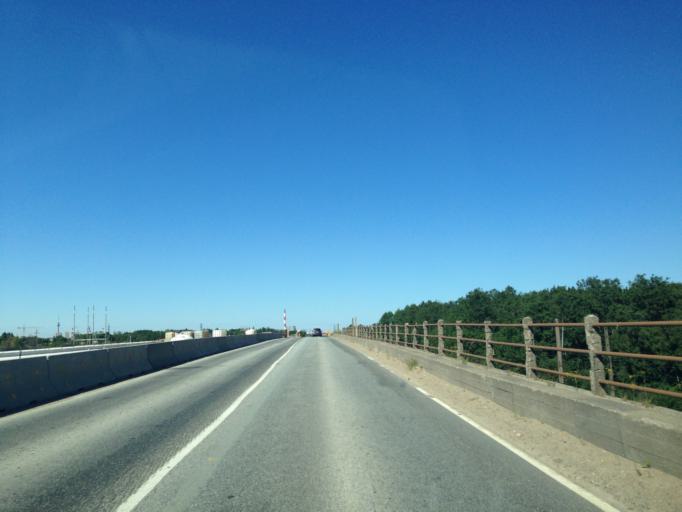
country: EE
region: Harju
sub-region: Joelaehtme vald
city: Loo
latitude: 59.4065
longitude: 24.9166
